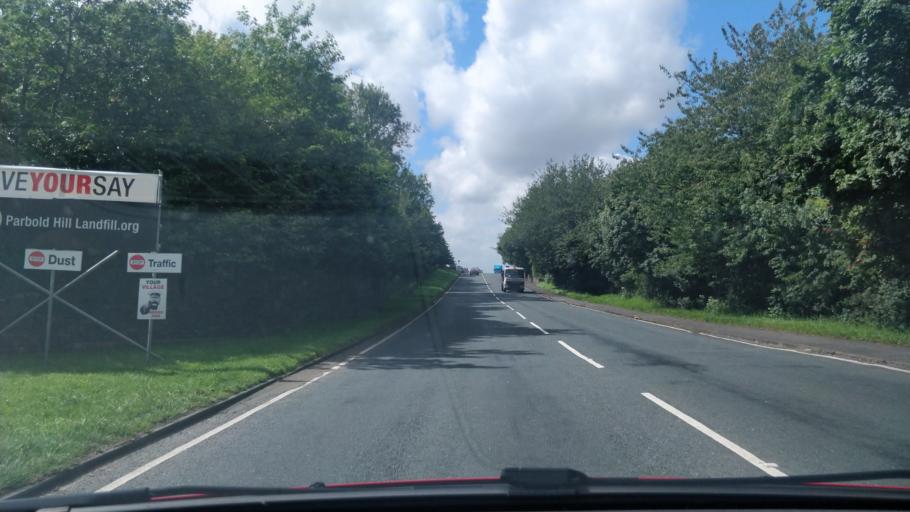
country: GB
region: England
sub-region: Lancashire
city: Appley Bridge
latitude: 53.5914
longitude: -2.7402
